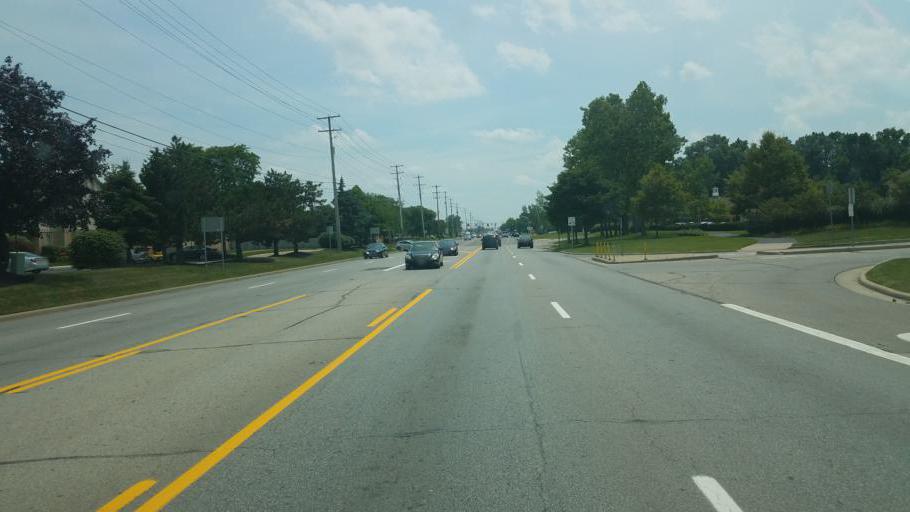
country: US
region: Ohio
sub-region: Franklin County
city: Dublin
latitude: 40.1211
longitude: -83.0903
